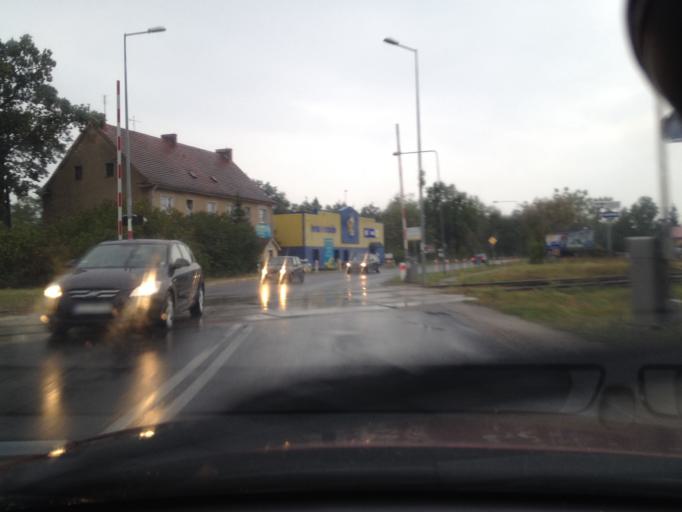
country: PL
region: Lubusz
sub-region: Powiat zaganski
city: Zagan
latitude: 51.6059
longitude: 15.2992
